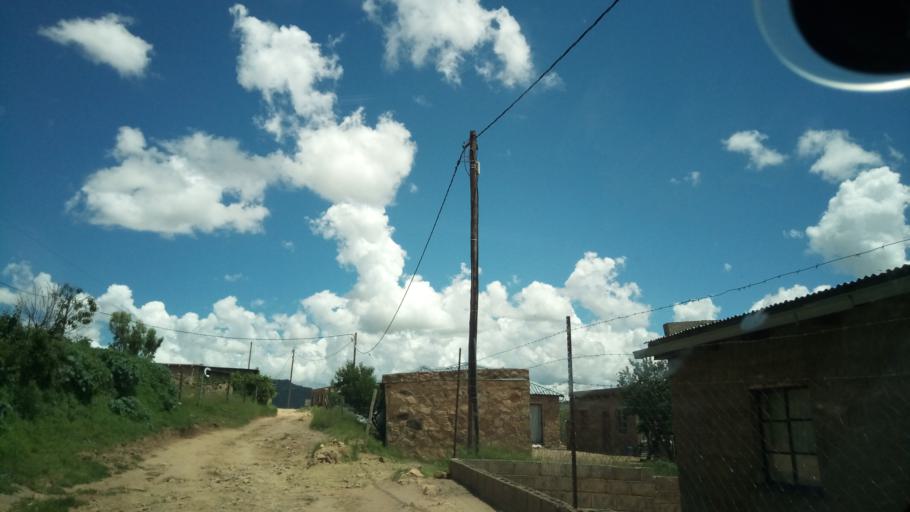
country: LS
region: Maseru
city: Maseru
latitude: -29.3510
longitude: 27.5295
